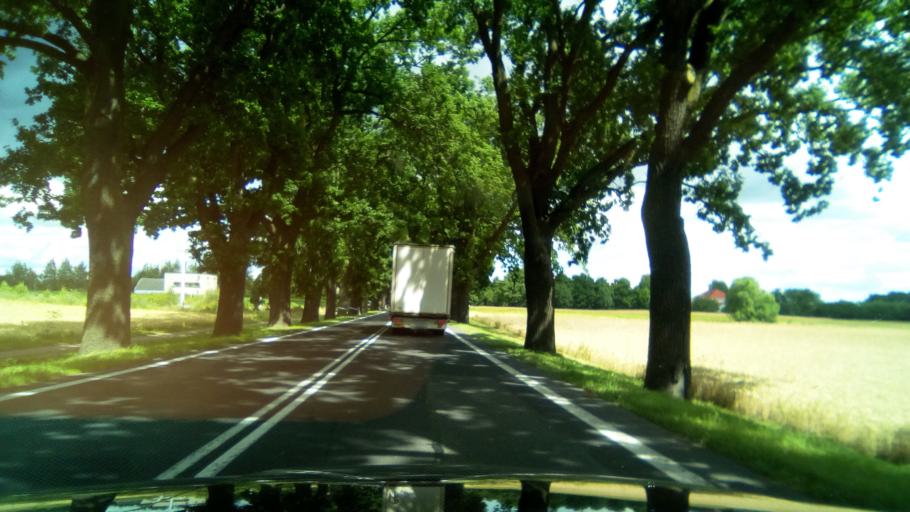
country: PL
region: Kujawsko-Pomorskie
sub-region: Powiat bydgoski
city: Osielsko
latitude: 53.2260
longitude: 18.1314
